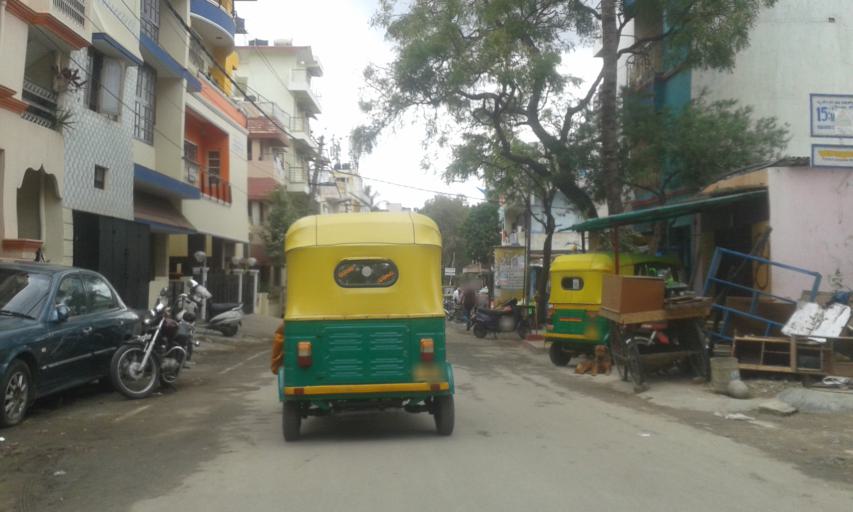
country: IN
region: Karnataka
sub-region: Bangalore Urban
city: Bangalore
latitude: 12.9660
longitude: 77.6442
